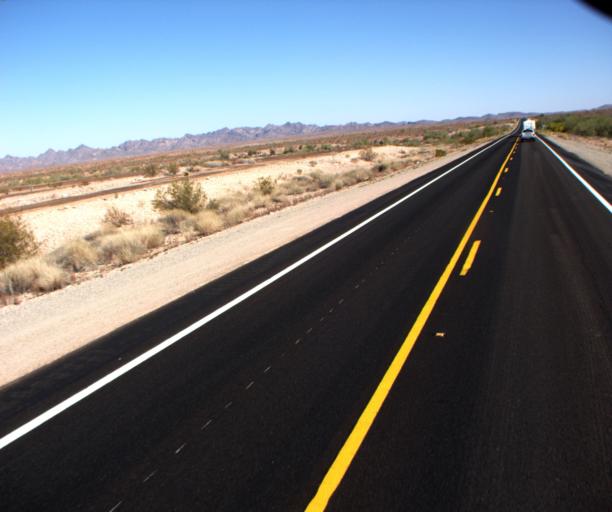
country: US
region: Arizona
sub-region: Yuma County
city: Wellton
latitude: 33.1356
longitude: -114.2875
